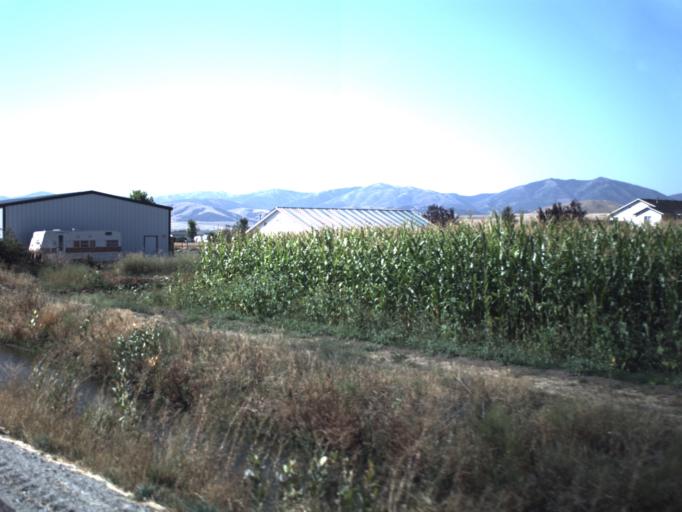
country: US
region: Utah
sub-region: Cache County
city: Hyrum
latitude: 41.6093
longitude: -111.8328
